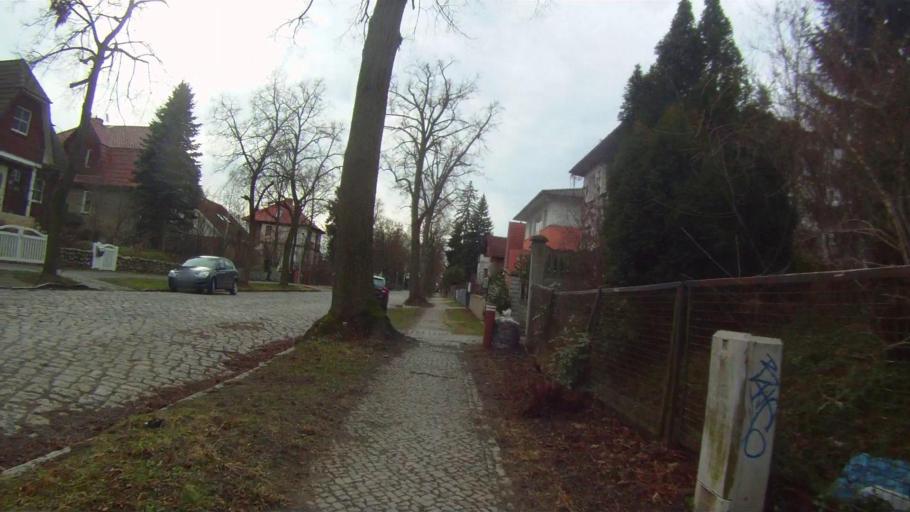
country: DE
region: Berlin
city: Lichtenrade
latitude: 52.3755
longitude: 13.3990
